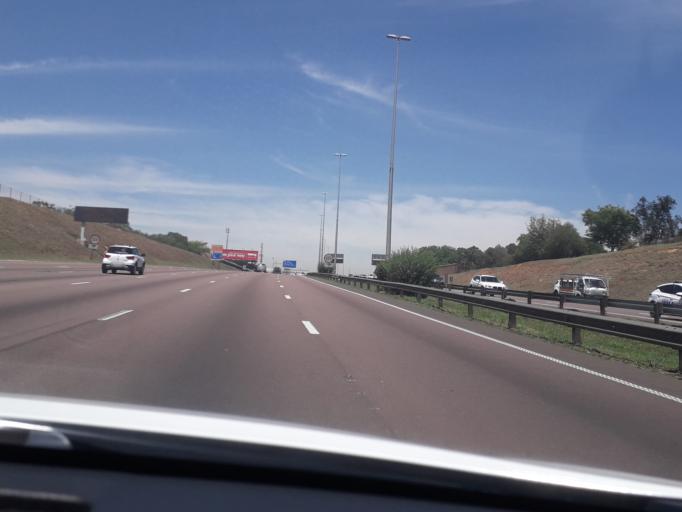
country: ZA
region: Gauteng
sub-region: City of Tshwane Metropolitan Municipality
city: Centurion
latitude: -25.8137
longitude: 28.2570
